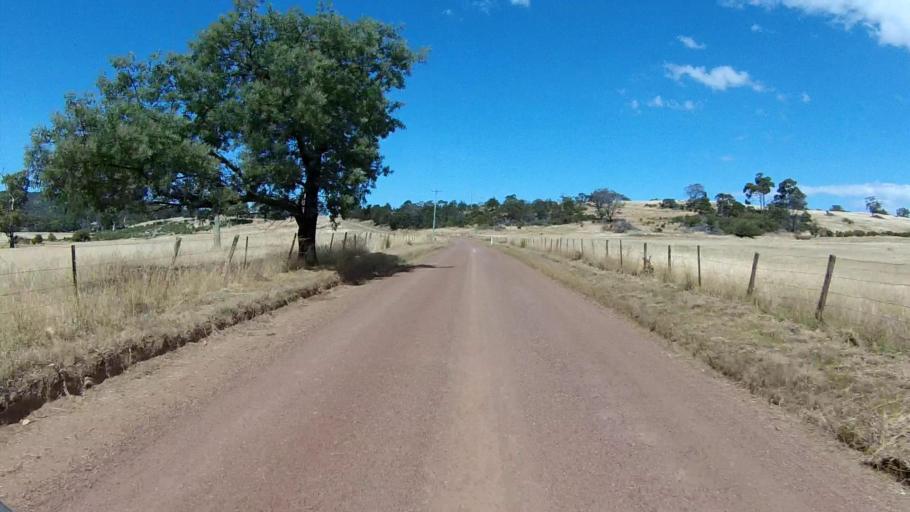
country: AU
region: Tasmania
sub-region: Break O'Day
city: St Helens
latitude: -41.9637
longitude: 148.0731
